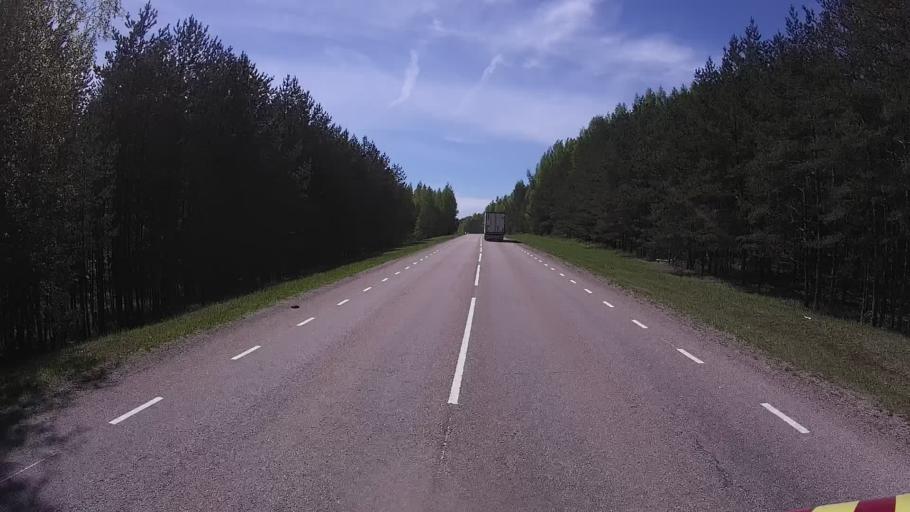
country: EE
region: Vorumaa
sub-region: Voru linn
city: Voru
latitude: 57.7737
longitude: 26.8655
